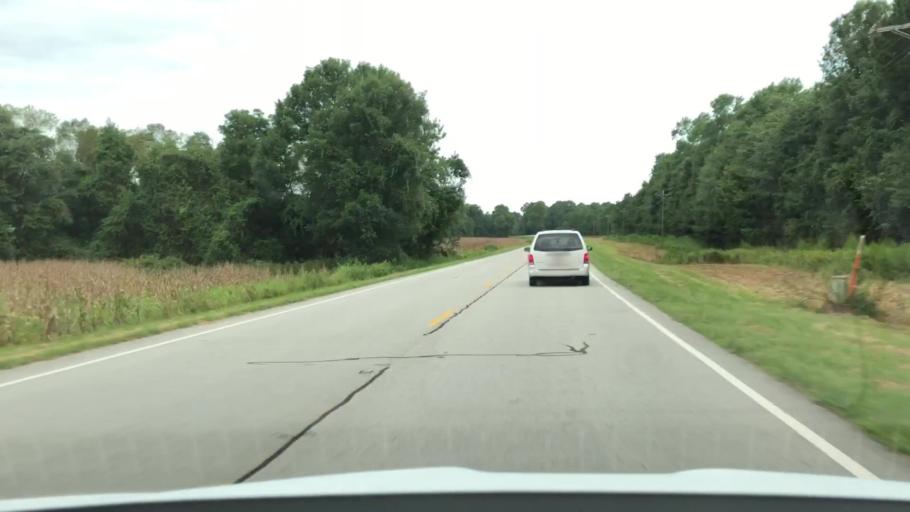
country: US
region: North Carolina
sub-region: Jones County
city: Trenton
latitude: 35.0788
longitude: -77.4120
